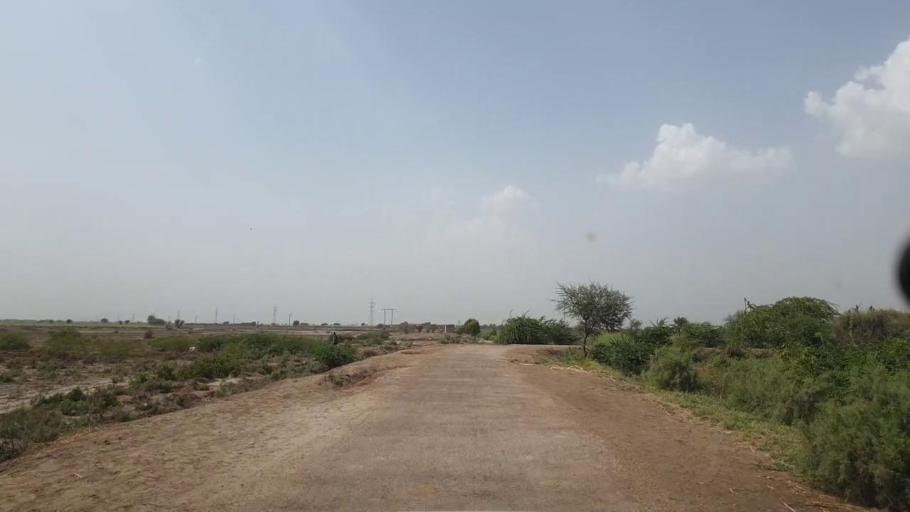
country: PK
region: Sindh
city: Tando Ghulam Ali
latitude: 25.0686
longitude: 68.8117
